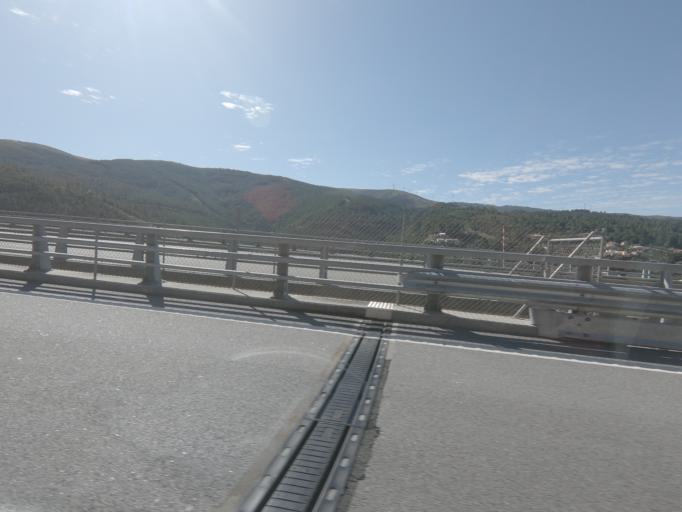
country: PT
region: Coimbra
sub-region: Oliveira do Hospital
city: Oliveira do Hospital
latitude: 40.3650
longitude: -7.8978
